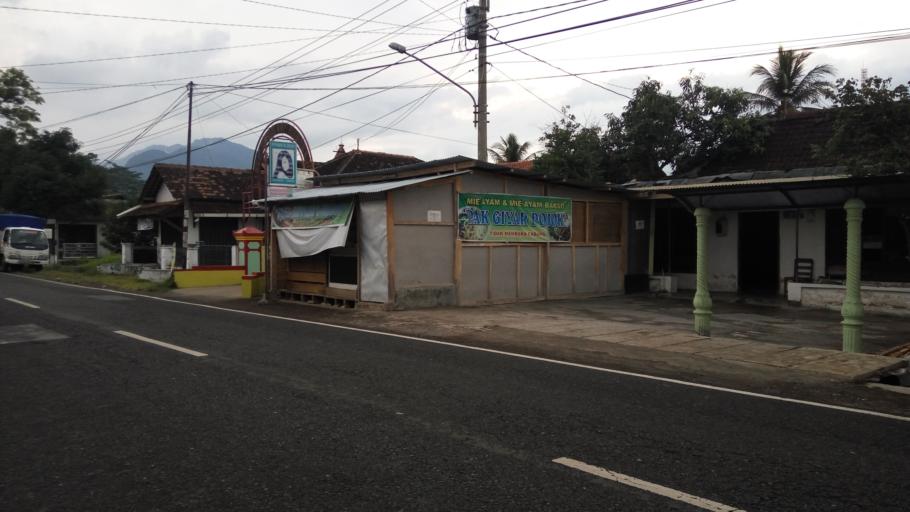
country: ID
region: Central Java
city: Ambarawa
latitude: -7.2708
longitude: 110.4025
